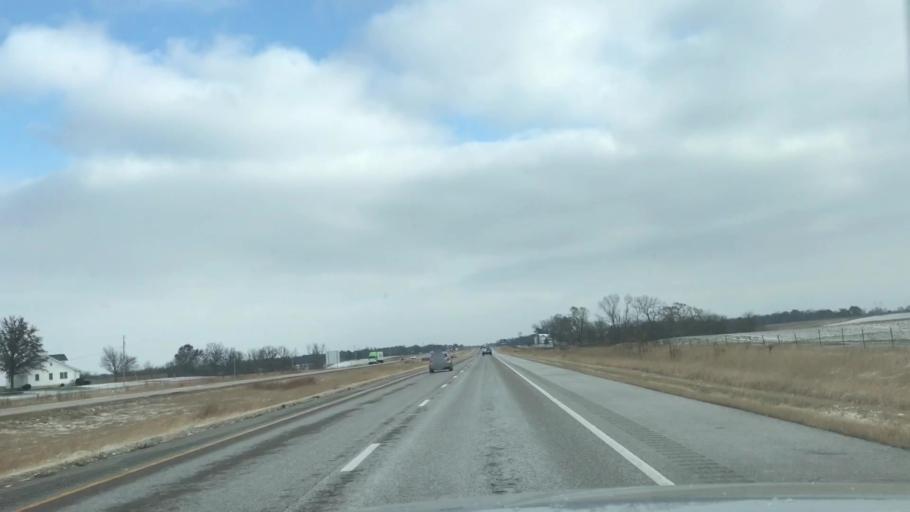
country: US
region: Illinois
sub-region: Madison County
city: Worden
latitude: 38.9457
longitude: -89.7825
